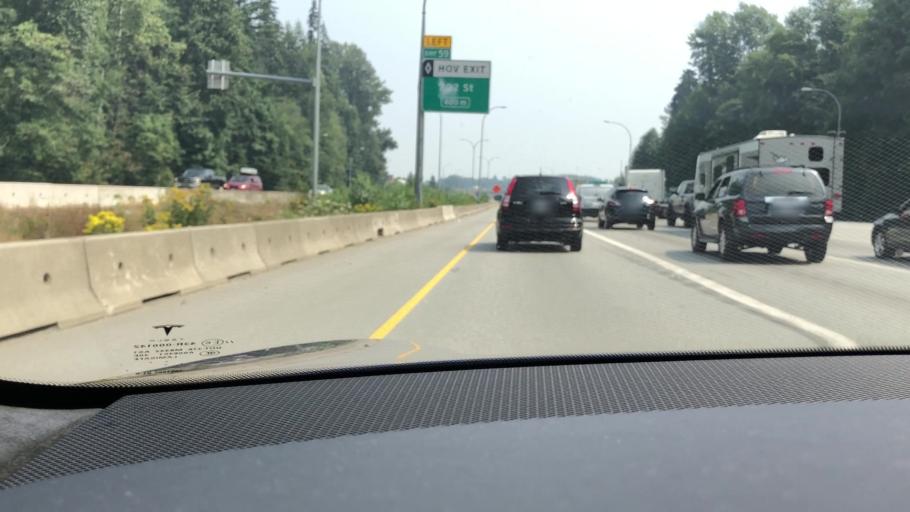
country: CA
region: British Columbia
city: Walnut Grove
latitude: 49.1660
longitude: -122.6763
